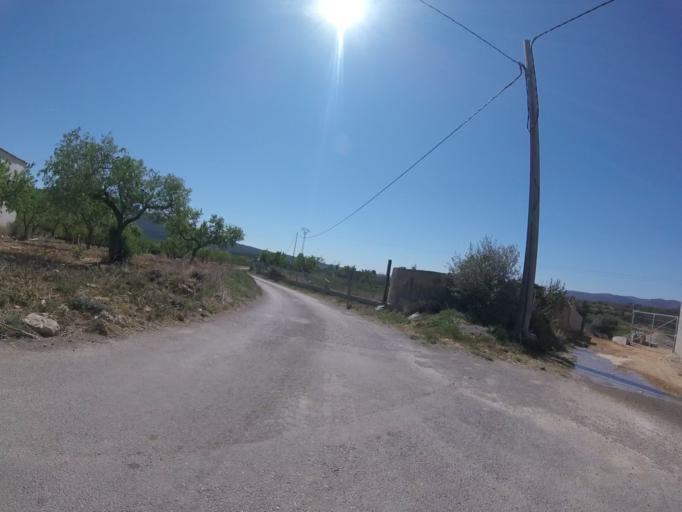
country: ES
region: Valencia
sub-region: Provincia de Castello
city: Cuevas de Vinroma
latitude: 40.3768
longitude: 0.1335
